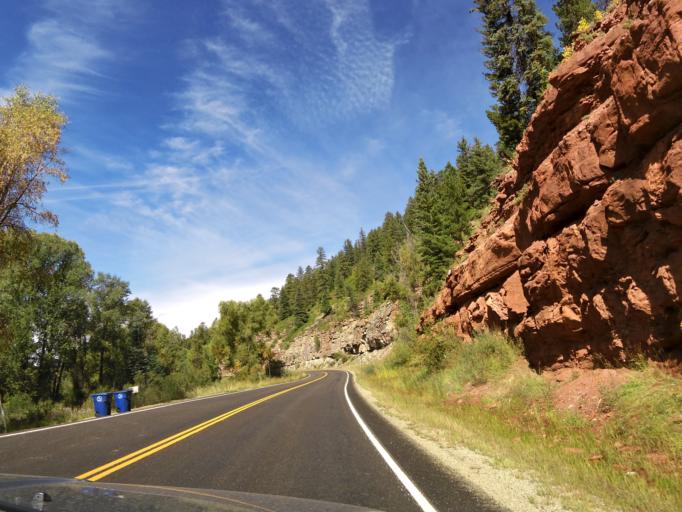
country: US
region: Colorado
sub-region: Montezuma County
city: Mancos
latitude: 37.5758
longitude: -108.1877
